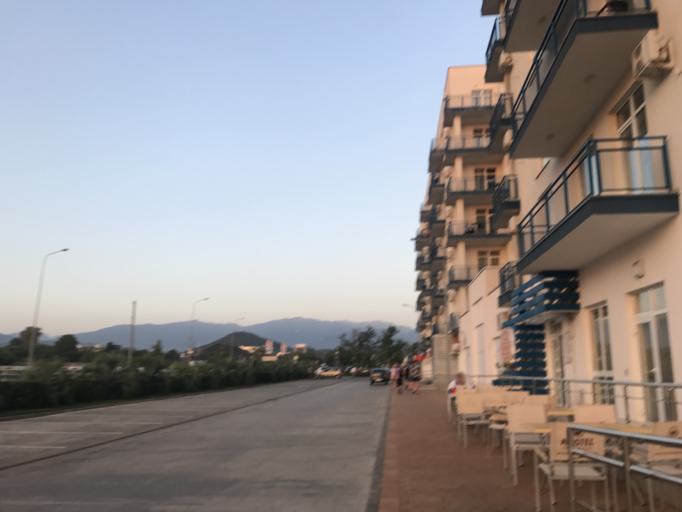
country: RU
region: Krasnodarskiy
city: Adler
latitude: 43.4137
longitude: 39.9332
